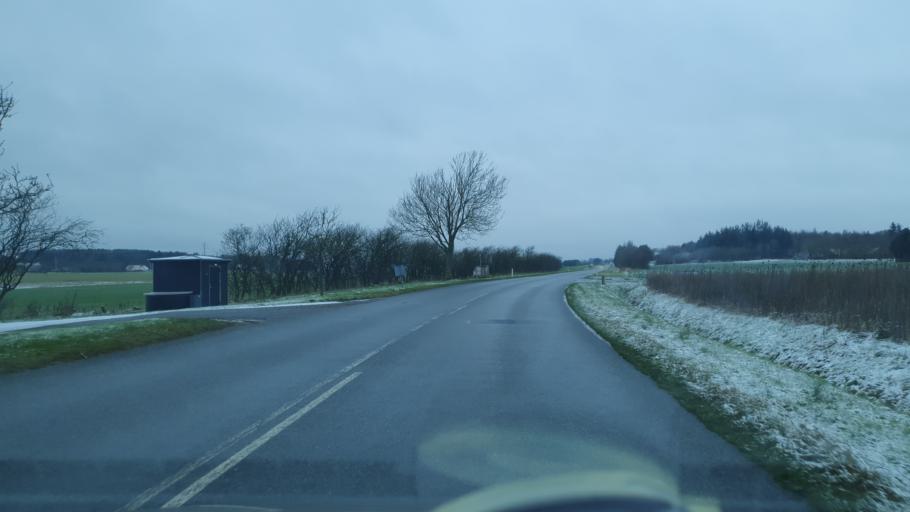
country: DK
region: North Denmark
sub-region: Jammerbugt Kommune
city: Brovst
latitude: 57.1028
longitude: 9.5033
